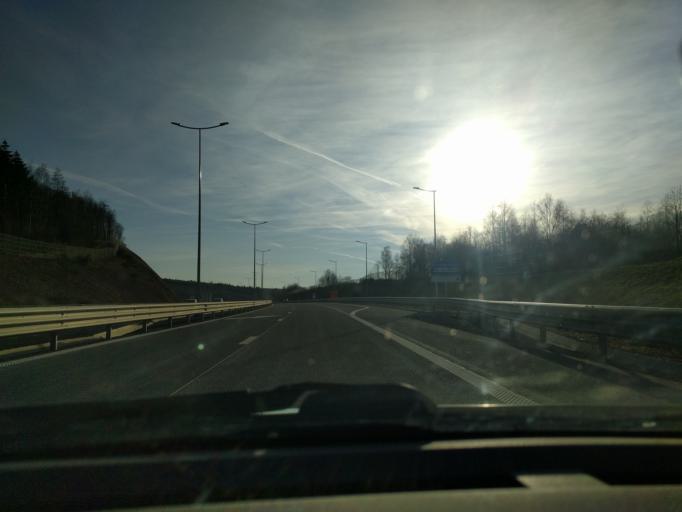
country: BE
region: Wallonia
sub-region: Province de Namur
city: Couvin
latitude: 50.0422
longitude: 4.5099
